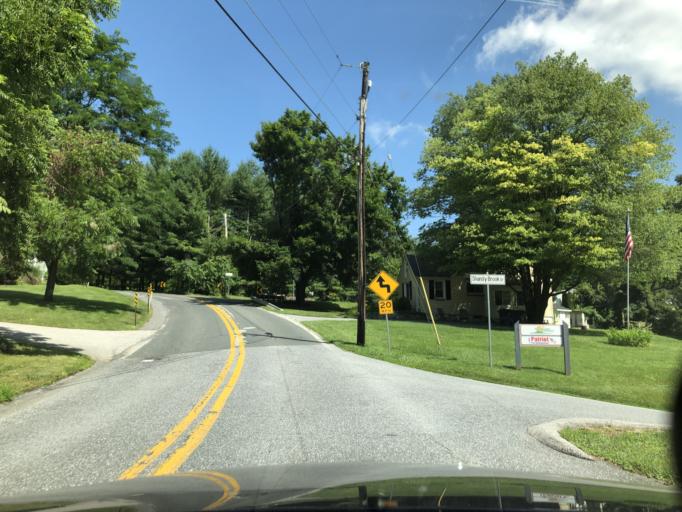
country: US
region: Maryland
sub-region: Carroll County
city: Westminster
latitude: 39.5922
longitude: -76.9687
